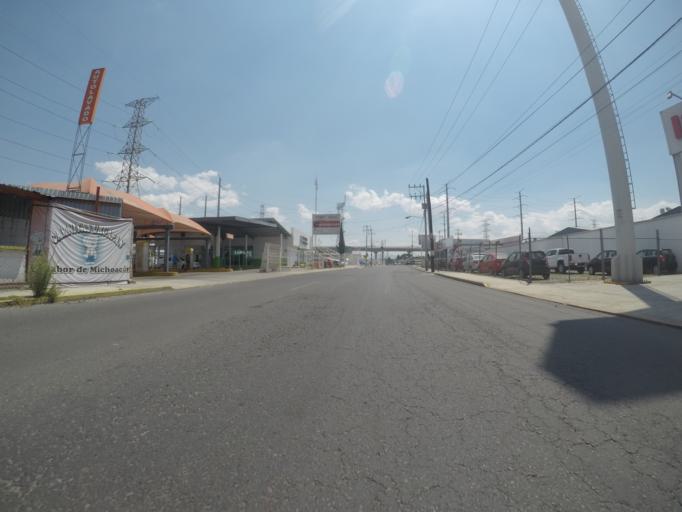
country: MX
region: Mexico
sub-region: Metepec
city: San Jorge Pueblo Nuevo
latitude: 19.2749
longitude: -99.6316
